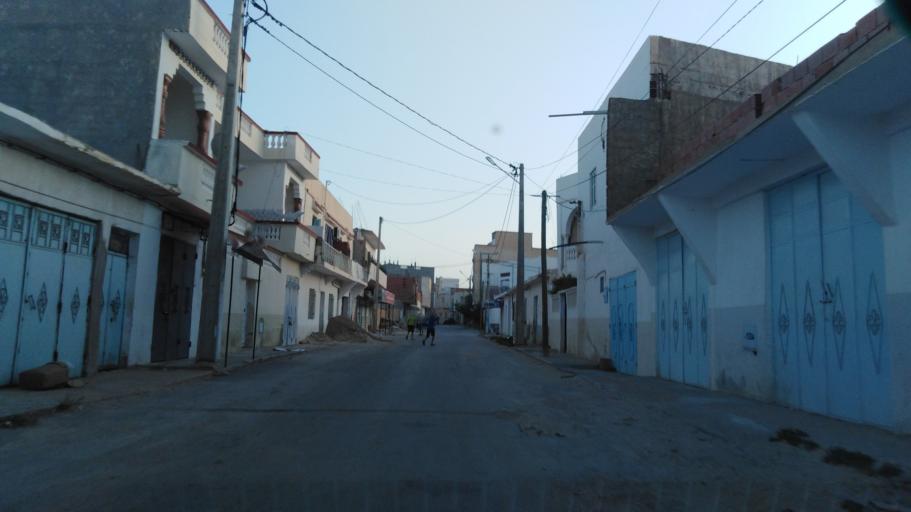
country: TN
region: Tataouine
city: Tataouine
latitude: 32.9363
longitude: 10.4549
